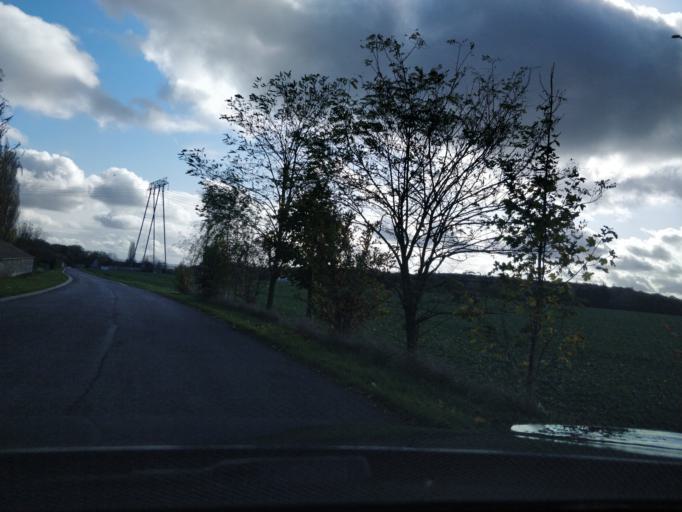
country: FR
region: Ile-de-France
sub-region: Departement de l'Essonne
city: Fontenay-les-Briis
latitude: 48.6374
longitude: 2.1537
